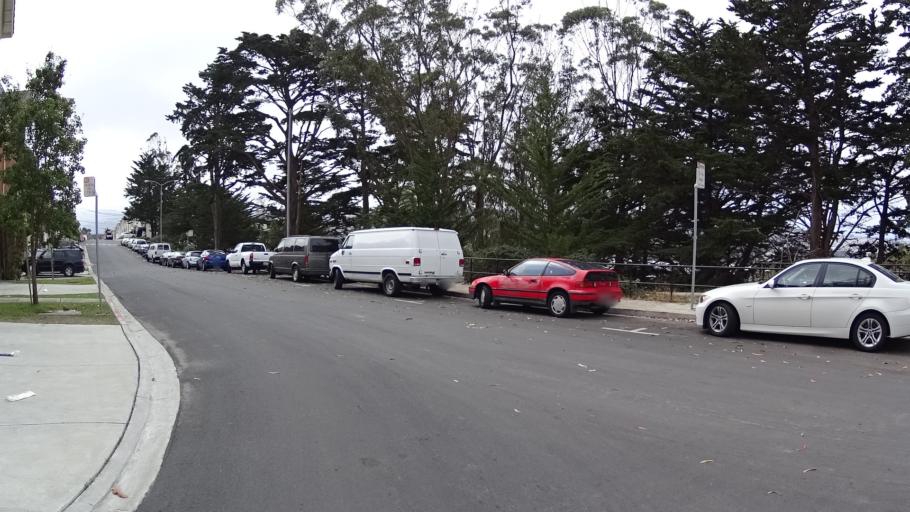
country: US
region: California
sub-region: San Mateo County
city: Daly City
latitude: 37.7013
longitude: -122.4594
